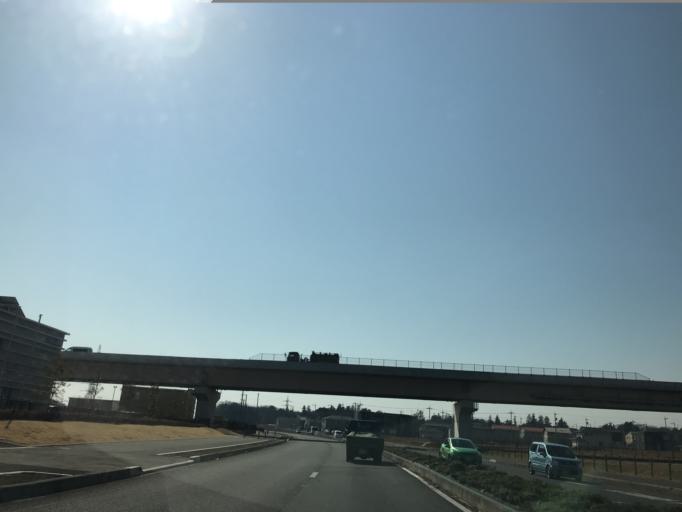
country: JP
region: Ibaraki
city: Mitsukaido
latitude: 36.0567
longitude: 140.0615
